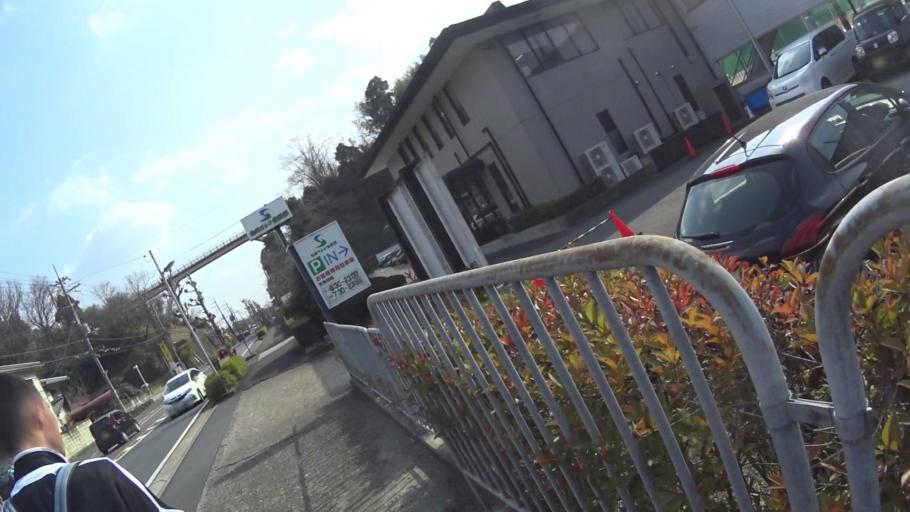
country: JP
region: Nara
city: Nara-shi
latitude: 34.7030
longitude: 135.8271
